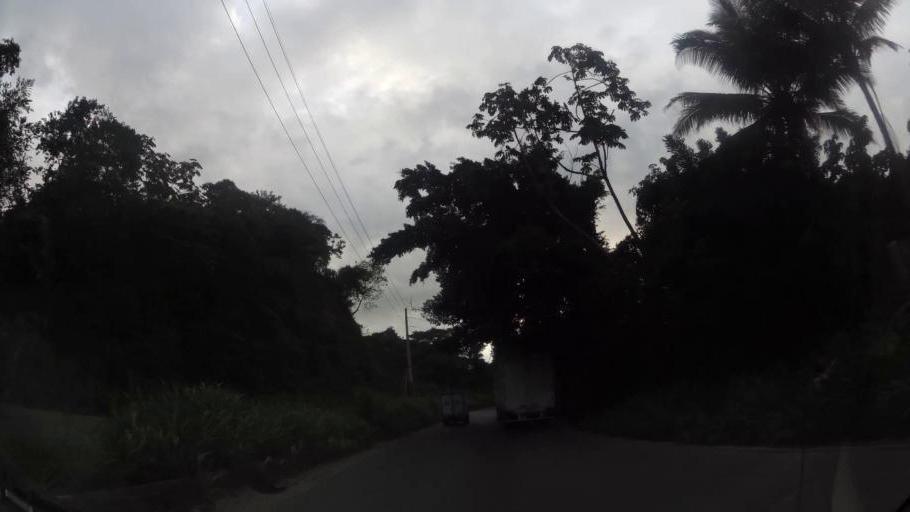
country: GT
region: Suchitepeque
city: Patulul
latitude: 14.3637
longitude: -91.0983
